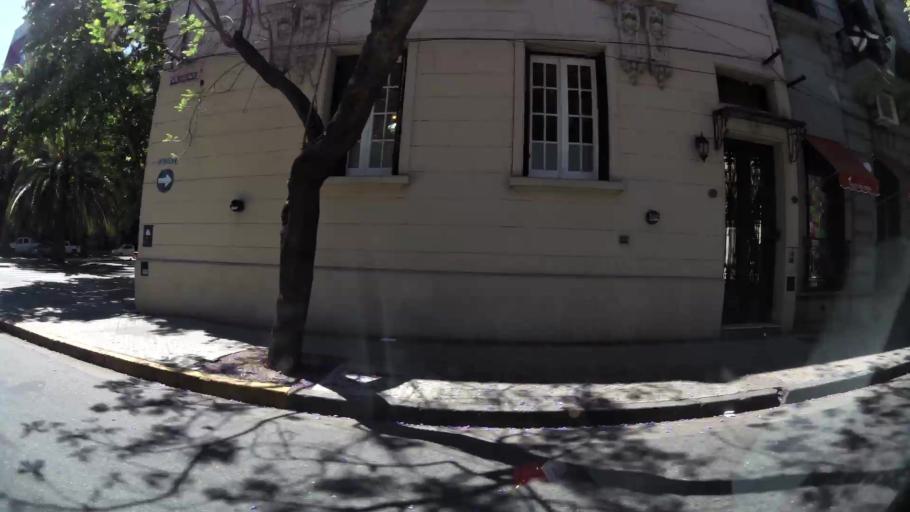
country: AR
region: Santa Fe
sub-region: Departamento de Rosario
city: Rosario
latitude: -32.9414
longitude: -60.6525
